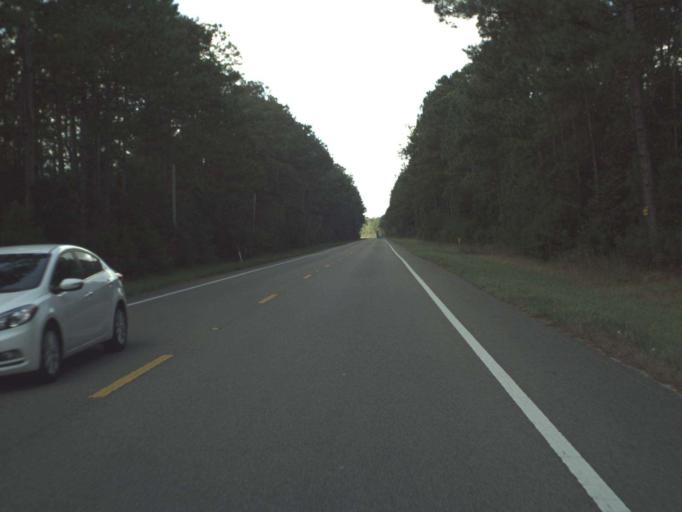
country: US
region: Florida
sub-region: Walton County
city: Freeport
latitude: 30.4669
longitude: -85.9457
